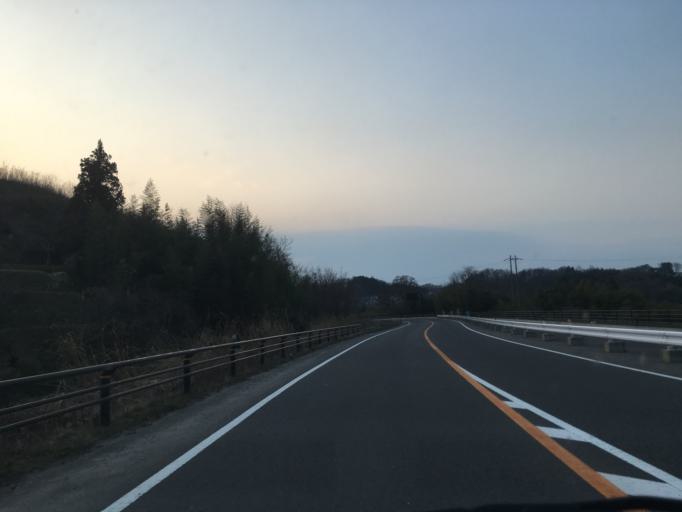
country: JP
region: Fukushima
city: Miharu
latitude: 37.4376
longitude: 140.4801
